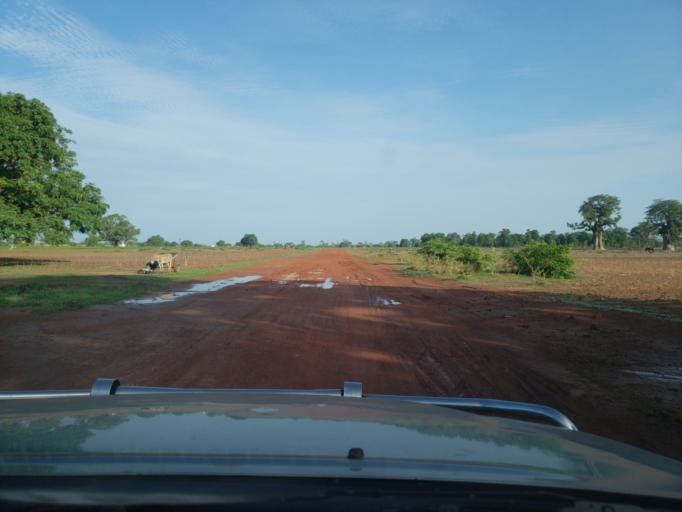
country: ML
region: Sikasso
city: Koutiala
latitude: 12.4288
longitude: -5.6042
